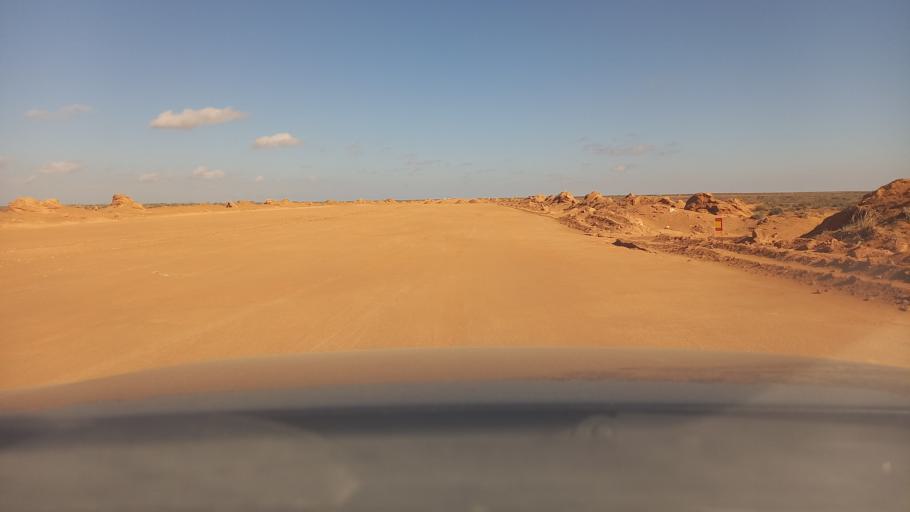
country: TN
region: Madanin
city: Medenine
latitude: 33.2372
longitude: 10.5526
